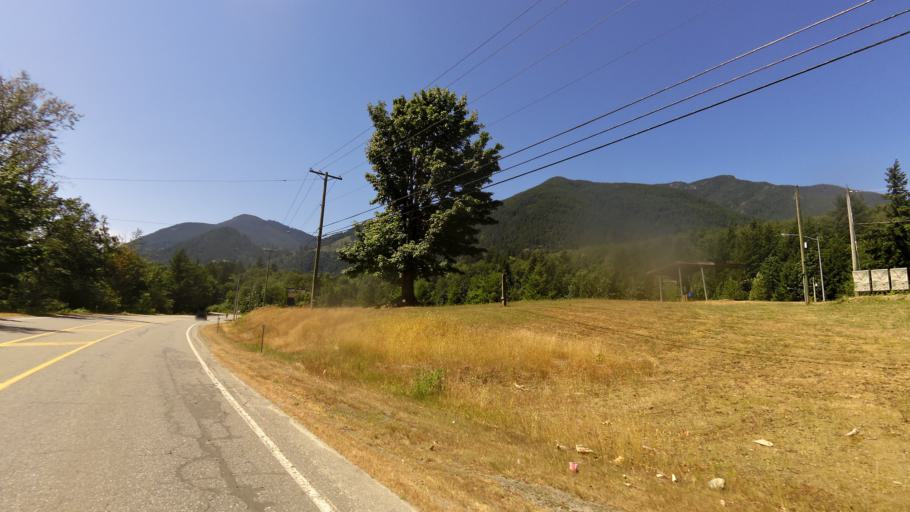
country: CA
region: British Columbia
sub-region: Fraser Valley Regional District
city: Chilliwack
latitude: 49.2029
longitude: -122.0305
